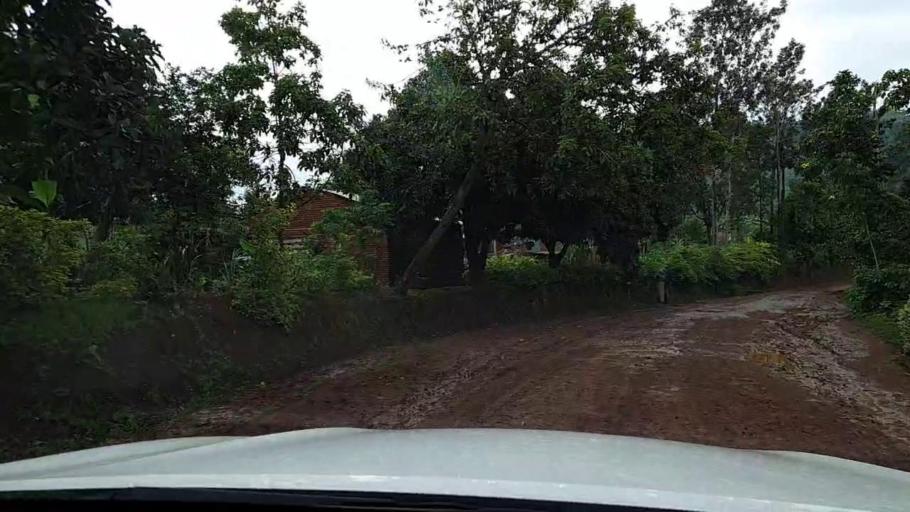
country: RW
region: Western Province
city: Cyangugu
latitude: -2.5659
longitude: 29.0334
